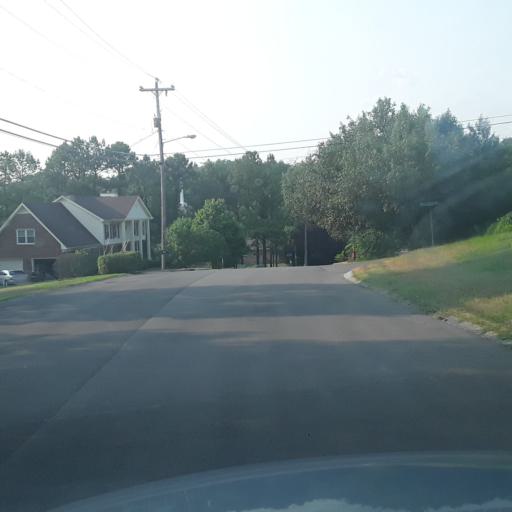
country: US
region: Tennessee
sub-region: Williamson County
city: Brentwood Estates
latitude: 36.0377
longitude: -86.7378
